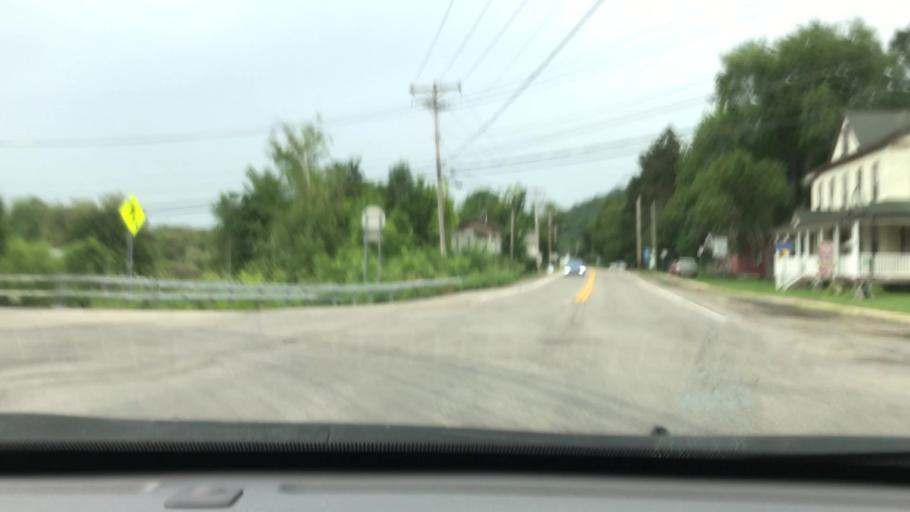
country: US
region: New York
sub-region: Cattaraugus County
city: Salamanca
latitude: 42.2143
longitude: -78.6366
